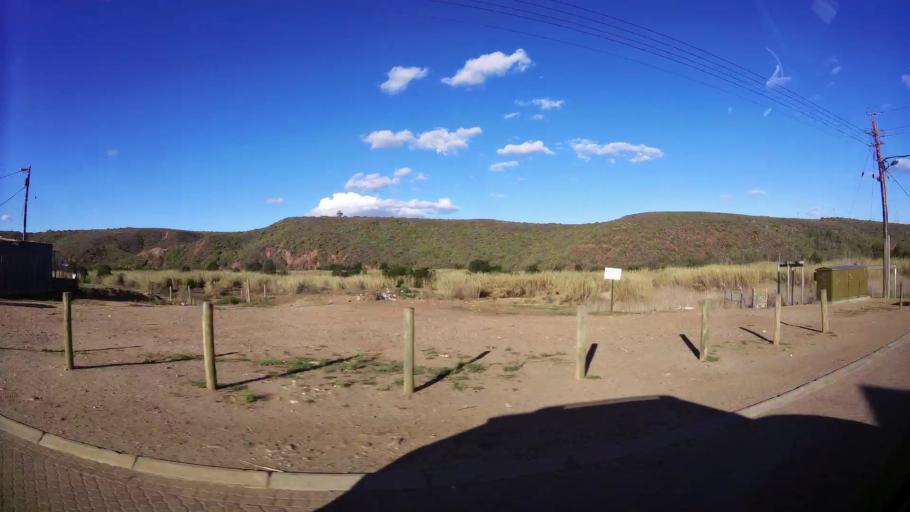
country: ZA
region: Western Cape
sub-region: Eden District Municipality
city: Riversdale
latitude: -34.1063
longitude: 20.9697
